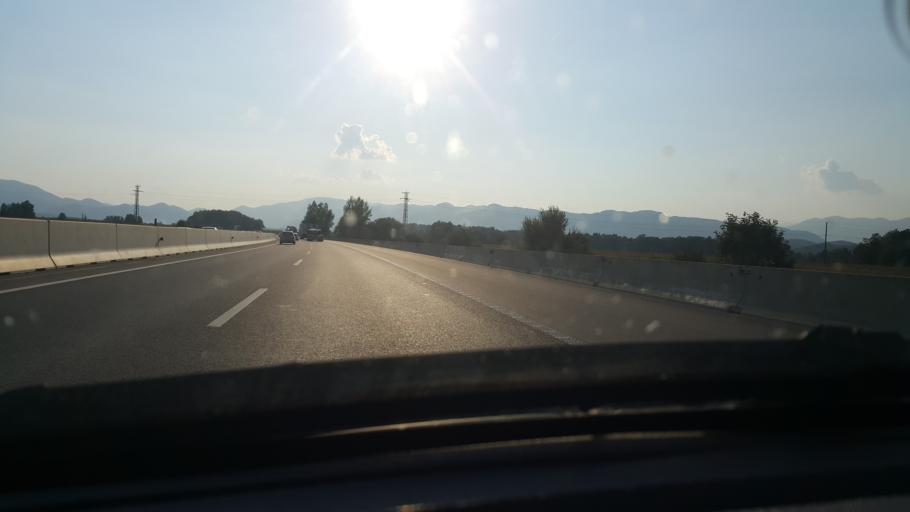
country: SI
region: Zalec
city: Sempeter v Savinj. Dolini
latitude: 46.2718
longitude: 15.1279
